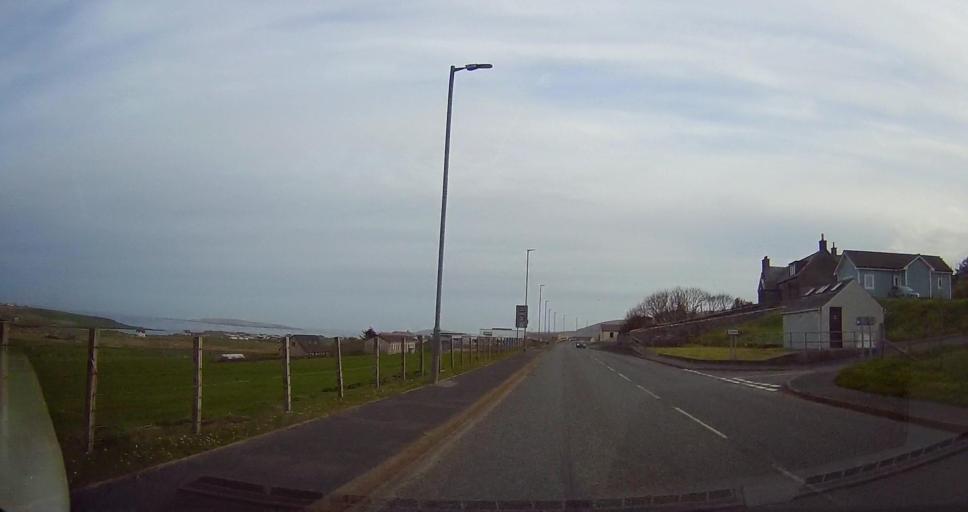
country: GB
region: Scotland
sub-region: Shetland Islands
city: Sandwick
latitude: 60.0480
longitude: -1.2276
